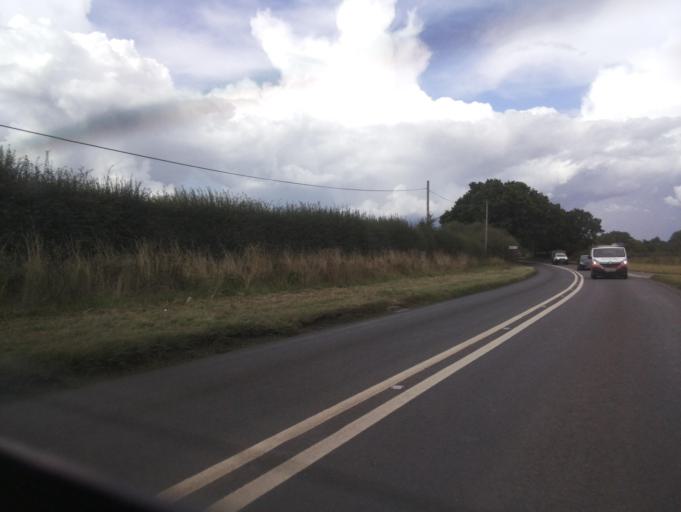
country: GB
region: England
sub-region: Telford and Wrekin
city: Newport
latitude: 52.8068
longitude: -2.3355
